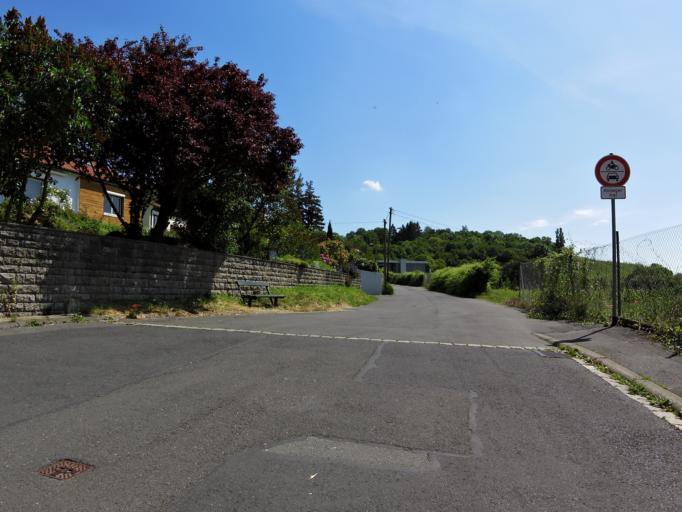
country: DE
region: Bavaria
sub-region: Regierungsbezirk Unterfranken
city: Wuerzburg
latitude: 49.7732
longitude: 9.9486
